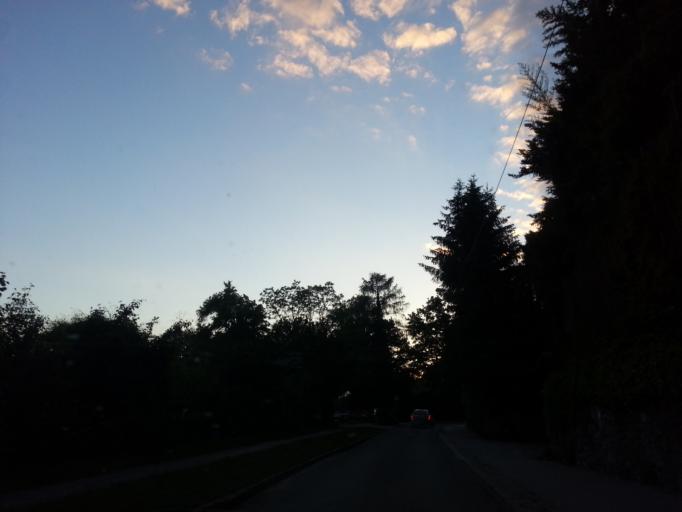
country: AT
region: Salzburg
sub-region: Salzburg Stadt
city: Salzburg
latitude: 47.7922
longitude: 13.0402
